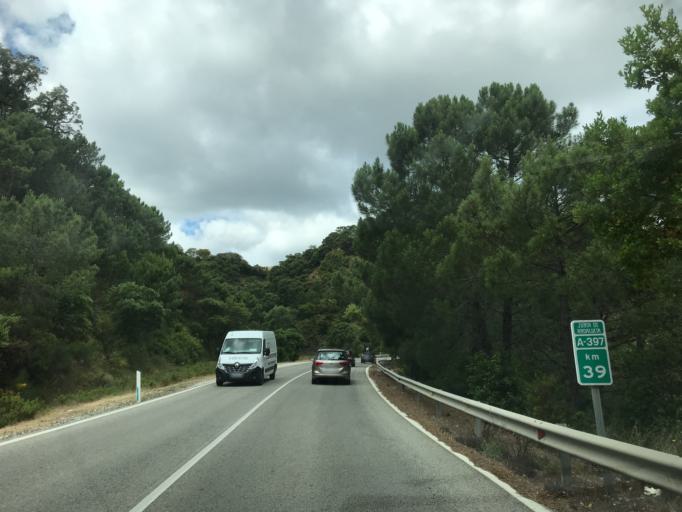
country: ES
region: Andalusia
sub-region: Provincia de Malaga
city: Benahavis
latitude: 36.5416
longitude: -5.0179
